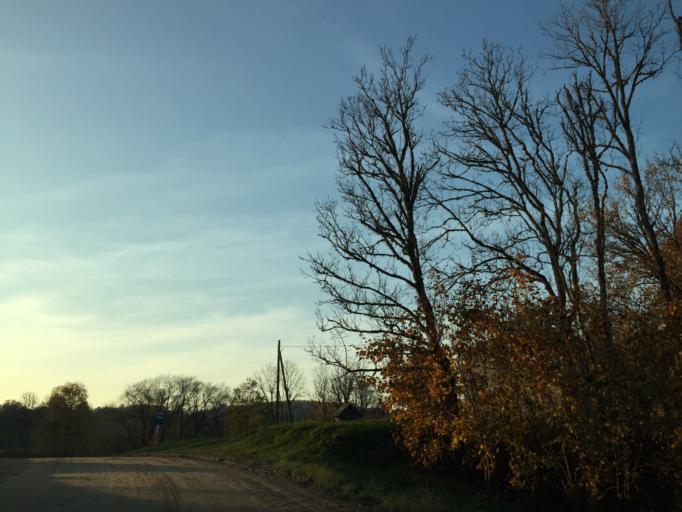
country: LV
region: Vainode
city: Vainode
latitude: 56.5058
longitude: 21.8195
